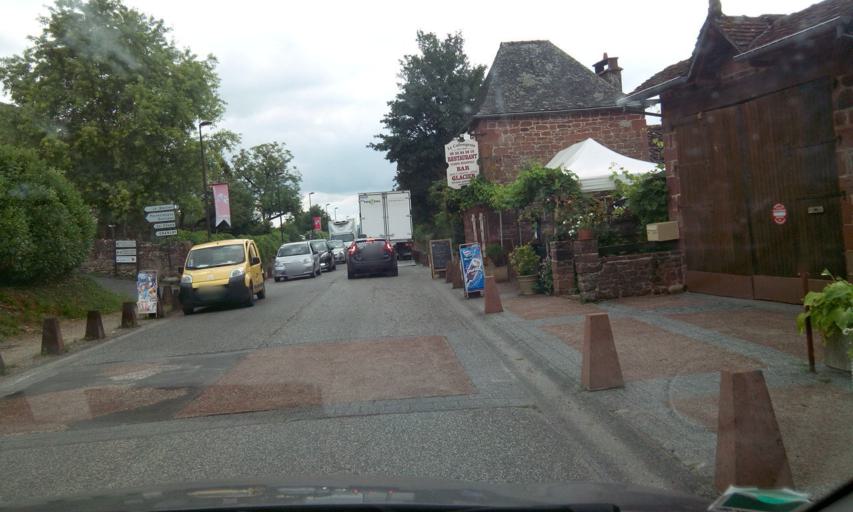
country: FR
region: Limousin
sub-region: Departement de la Correze
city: Meyssac
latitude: 45.0614
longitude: 1.6563
